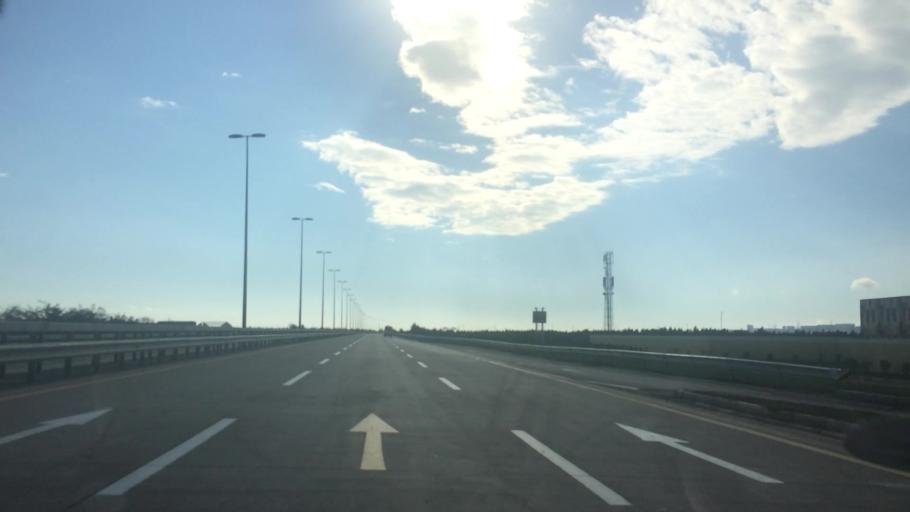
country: AZ
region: Baki
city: Hovsan
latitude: 40.3855
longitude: 50.0646
